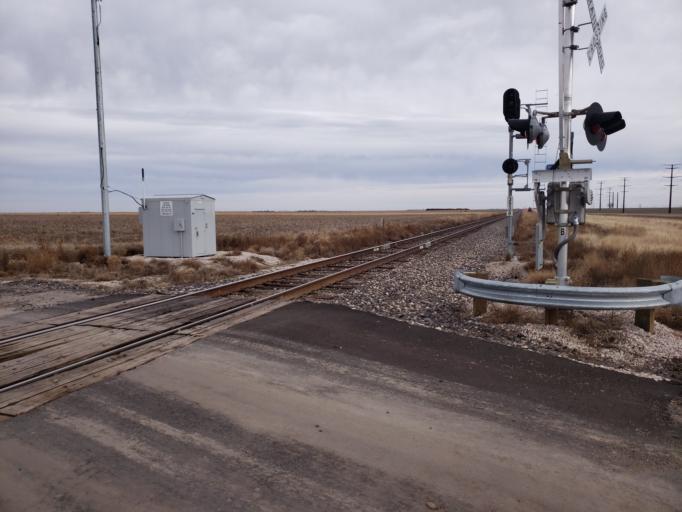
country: US
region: Kansas
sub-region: Clark County
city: Ashland
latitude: 37.5285
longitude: -99.7392
